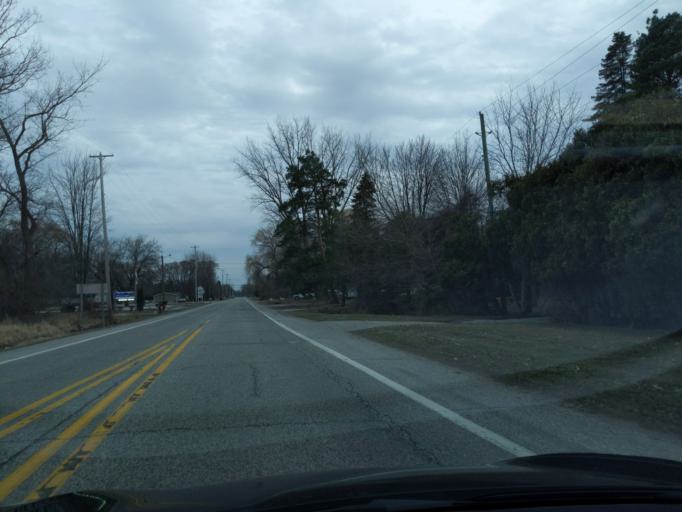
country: US
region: Michigan
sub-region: Bay County
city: Bay City
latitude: 43.6659
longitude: -83.9123
